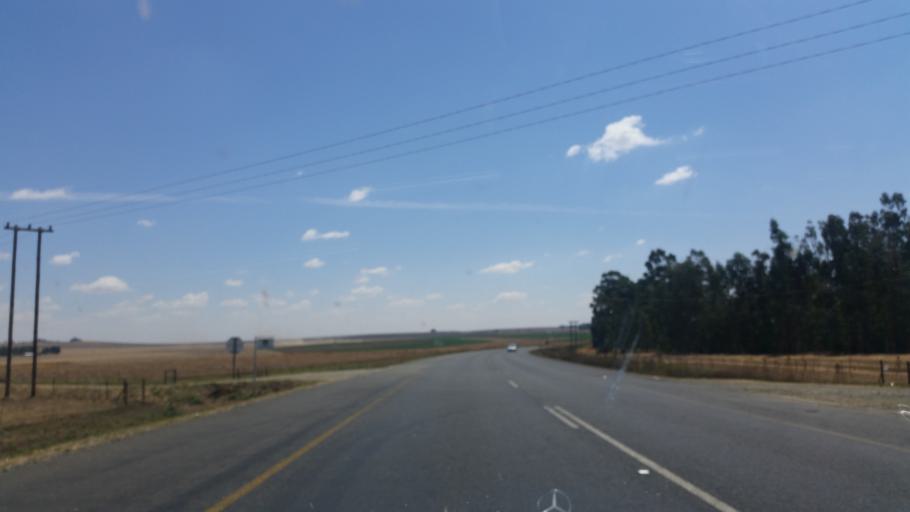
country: ZA
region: Orange Free State
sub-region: Thabo Mofutsanyana District Municipality
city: Bethlehem
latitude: -28.1057
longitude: 28.6622
